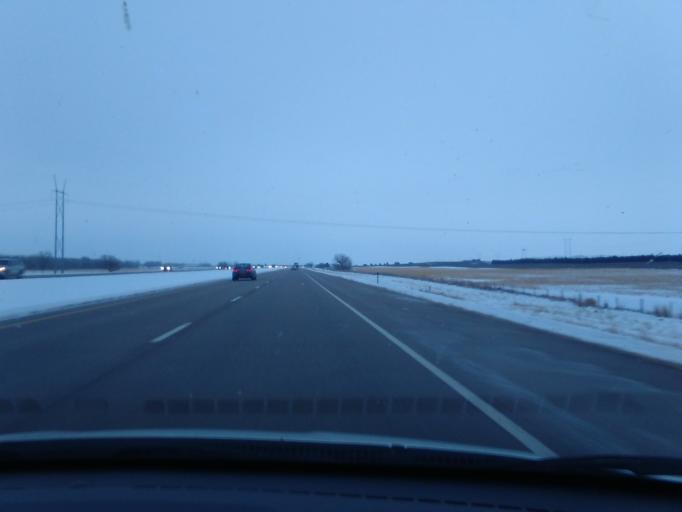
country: US
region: Nebraska
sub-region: Lincoln County
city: Sutherland
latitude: 41.1083
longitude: -101.3788
